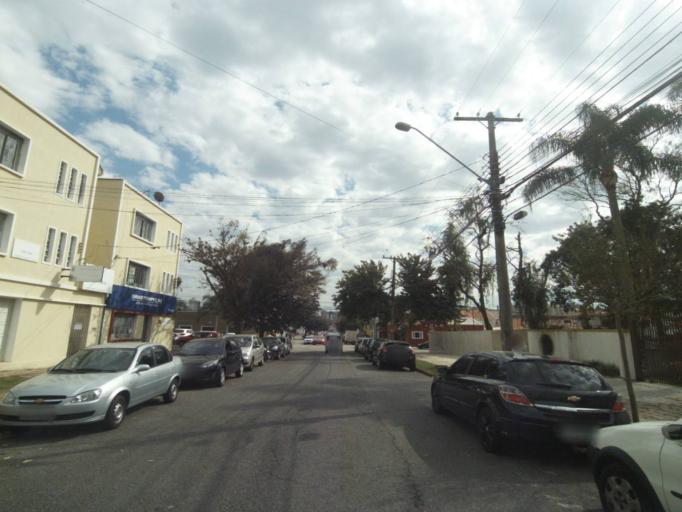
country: BR
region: Parana
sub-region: Curitiba
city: Curitiba
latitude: -25.4468
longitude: -49.2629
